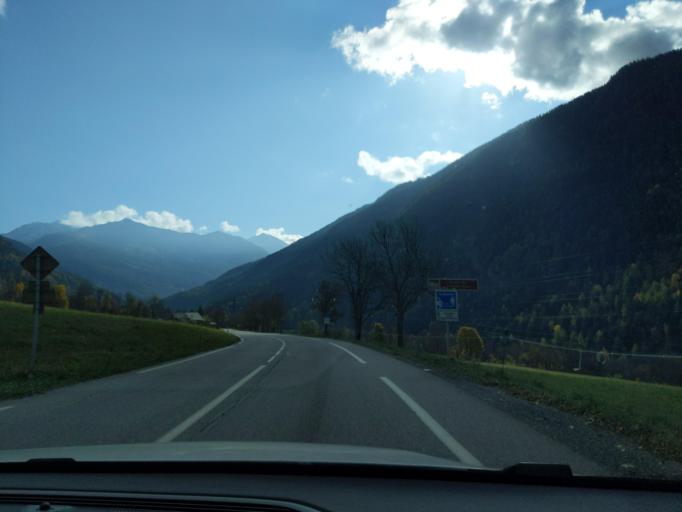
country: FR
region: Rhone-Alpes
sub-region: Departement de la Savoie
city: Seez
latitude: 45.6201
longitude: 6.8034
